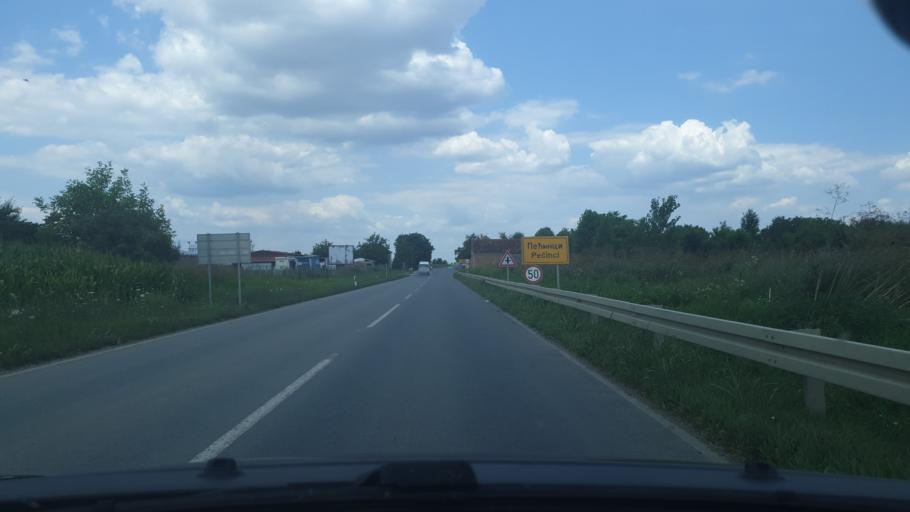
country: RS
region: Autonomna Pokrajina Vojvodina
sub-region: Sremski Okrug
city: Pecinci
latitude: 44.9059
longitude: 19.9564
